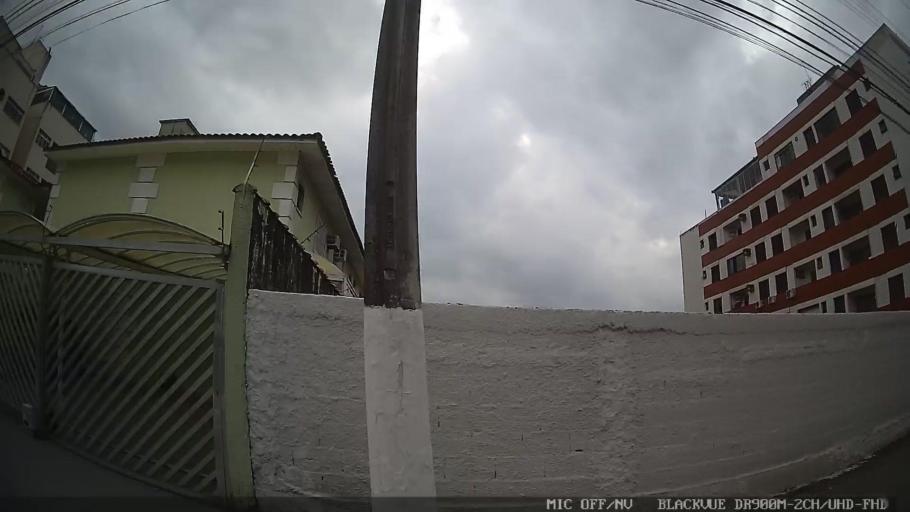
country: BR
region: Sao Paulo
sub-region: Guaruja
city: Guaruja
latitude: -24.0090
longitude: -46.2757
